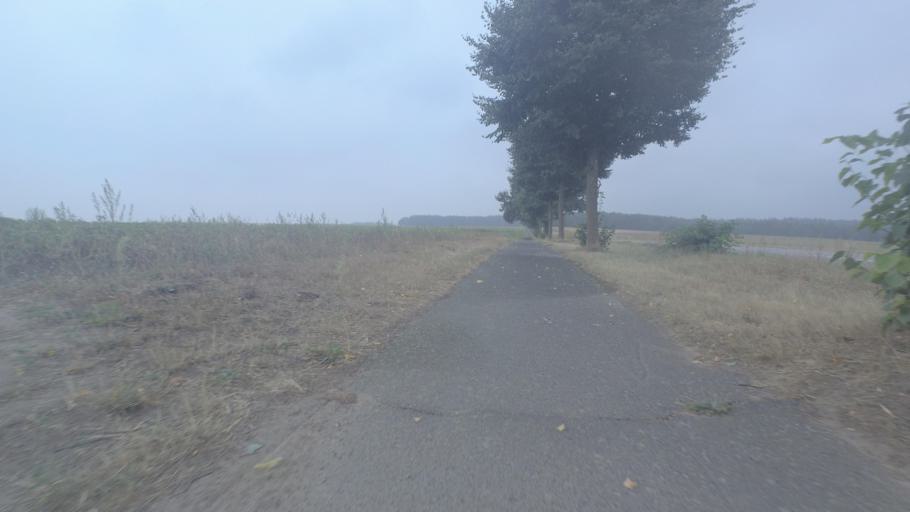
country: DE
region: Brandenburg
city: Heiligengrabe
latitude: 53.1397
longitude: 12.3686
